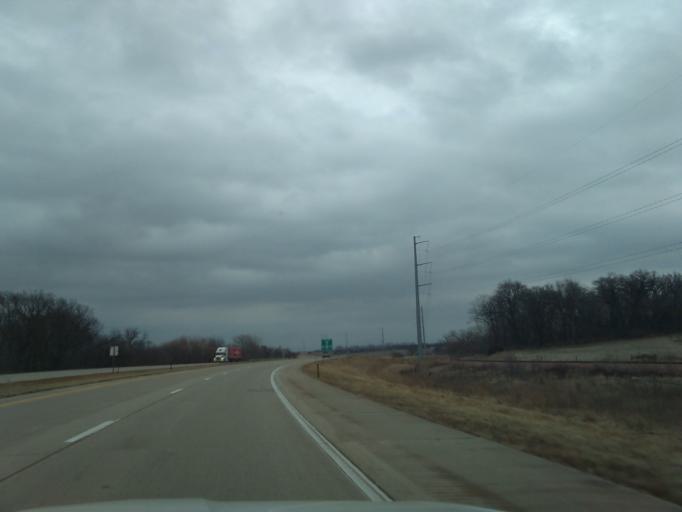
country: US
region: Nebraska
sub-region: Otoe County
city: Syracuse
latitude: 40.6770
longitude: -96.0358
